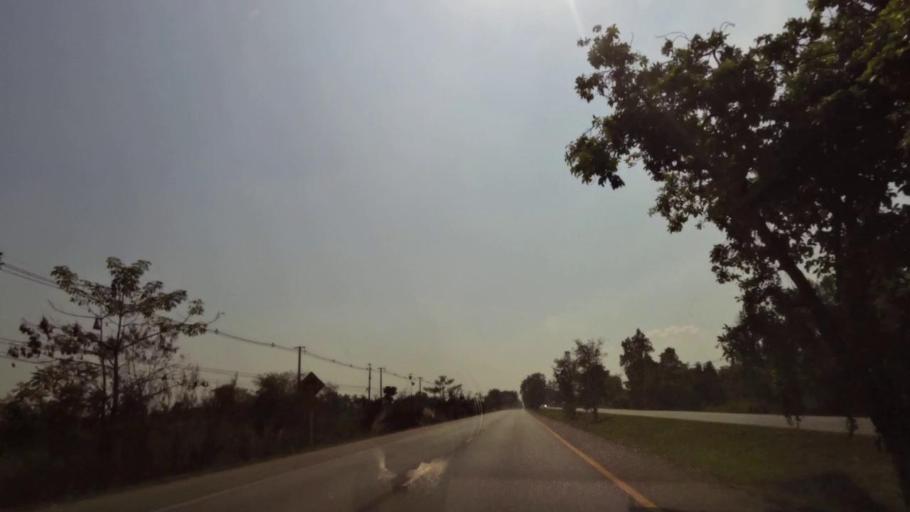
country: TH
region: Phichit
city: Bueng Na Rang
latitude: 16.2932
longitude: 100.1281
